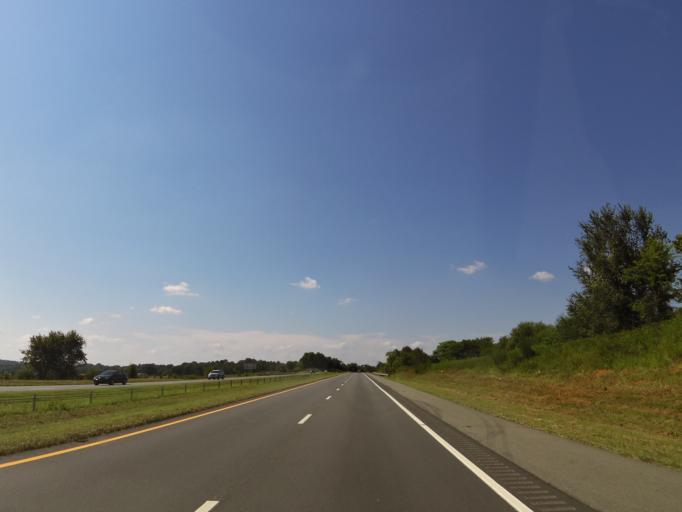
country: US
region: North Carolina
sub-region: Catawba County
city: Maiden
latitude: 35.5443
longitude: -81.2338
